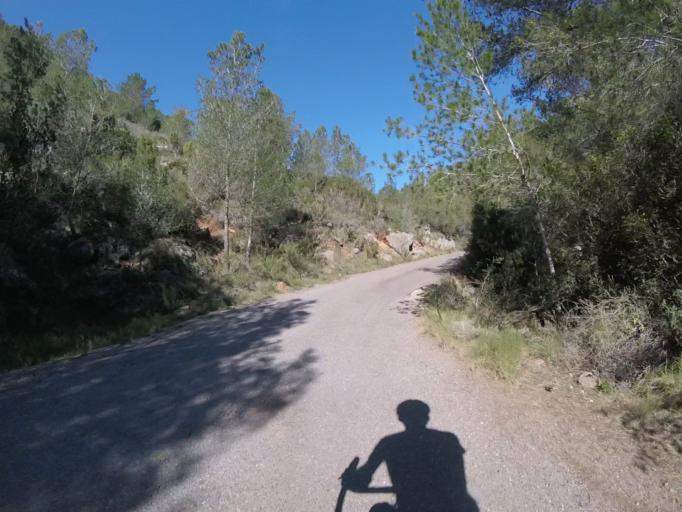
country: ES
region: Valencia
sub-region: Provincia de Castello
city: Benicassim
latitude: 40.0791
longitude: 0.1022
